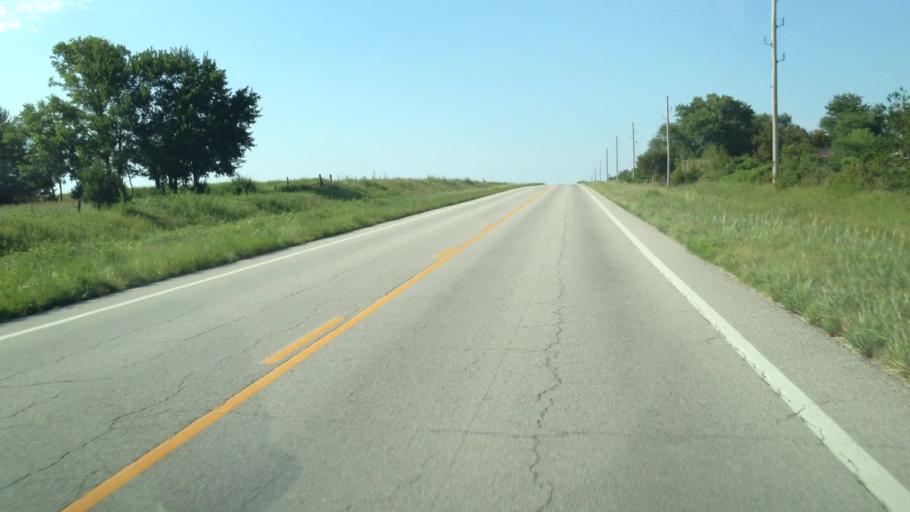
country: US
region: Kansas
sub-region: Allen County
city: Iola
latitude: 37.9971
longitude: -95.1704
